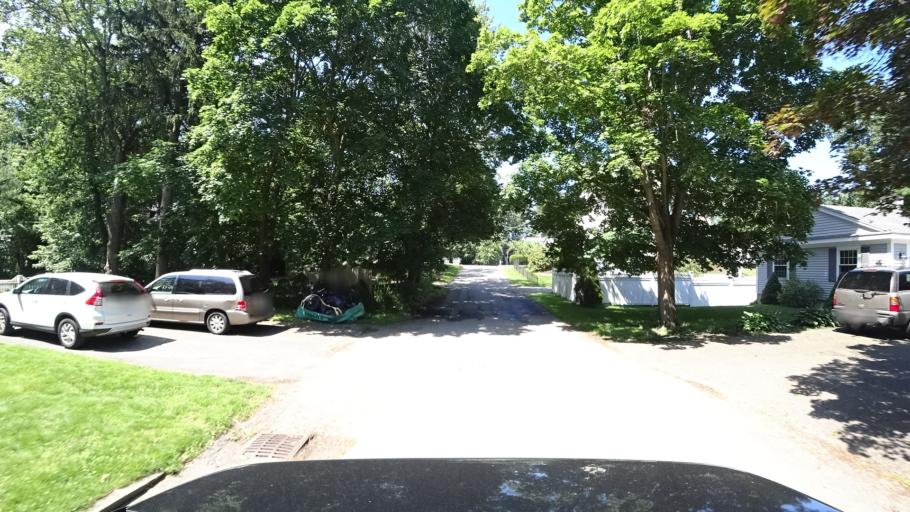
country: US
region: Massachusetts
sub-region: Norfolk County
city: Dedham
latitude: 42.2430
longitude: -71.1616
